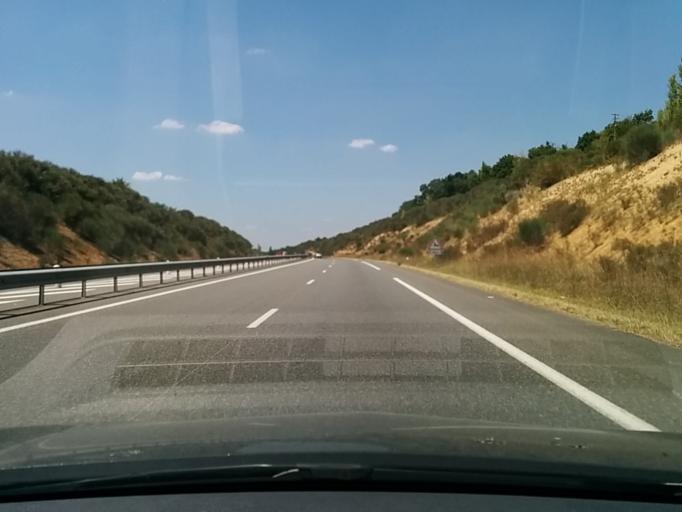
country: FR
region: Midi-Pyrenees
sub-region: Departement du Gers
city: Aubiet
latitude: 43.6392
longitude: 0.8196
